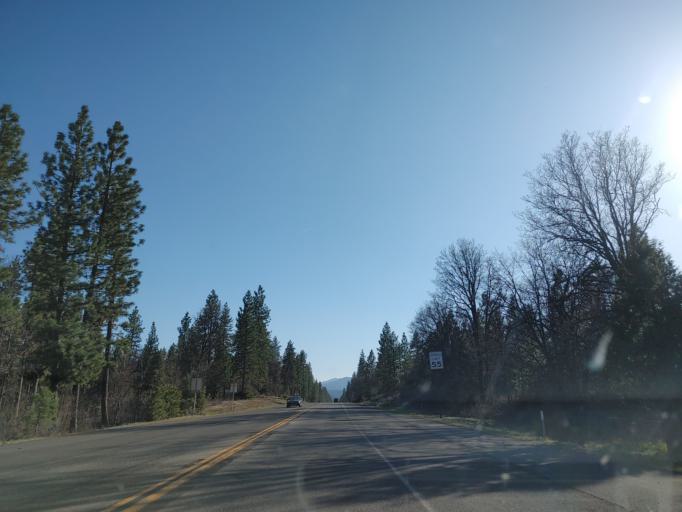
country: US
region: California
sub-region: Shasta County
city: Burney
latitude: 40.9121
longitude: -121.6324
